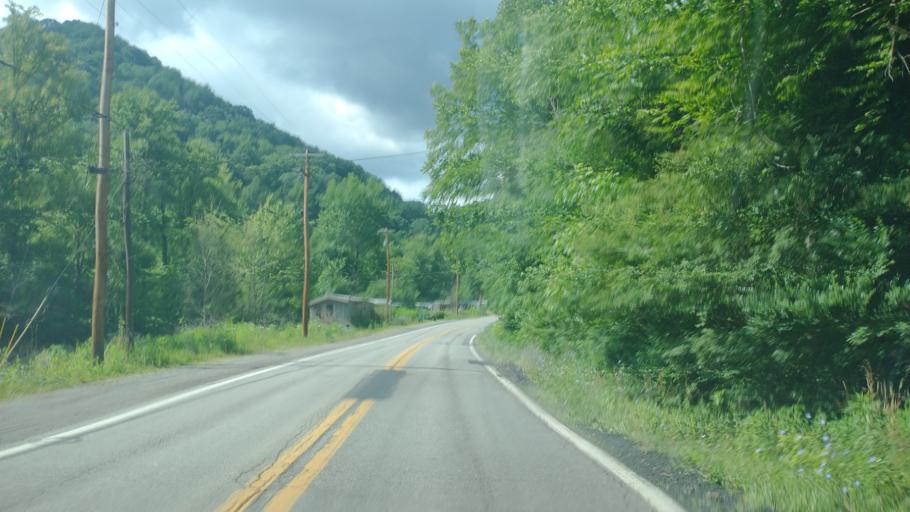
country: US
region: West Virginia
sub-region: McDowell County
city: Welch
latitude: 37.4183
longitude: -81.5186
